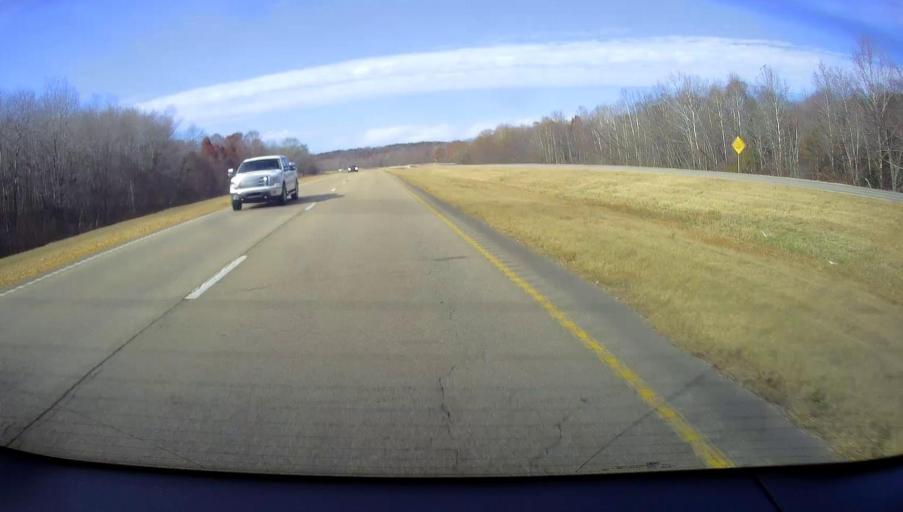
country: US
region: Mississippi
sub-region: Alcorn County
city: Corinth
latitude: 34.9418
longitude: -88.7827
